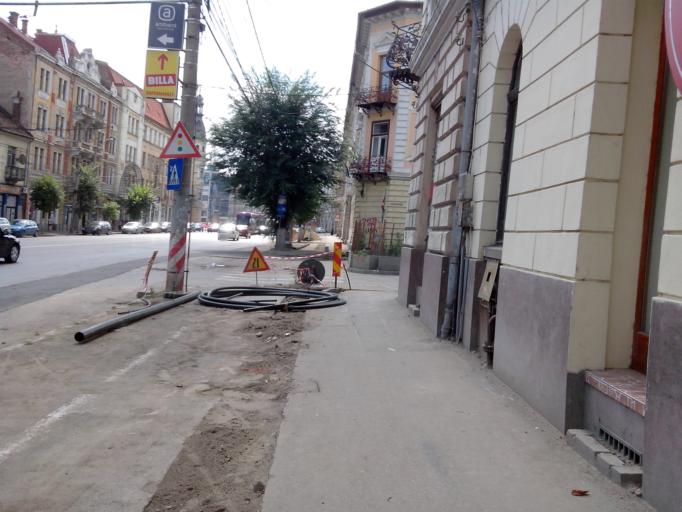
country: RO
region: Cluj
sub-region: Municipiul Cluj-Napoca
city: Cluj-Napoca
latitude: 46.7760
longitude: 23.5870
